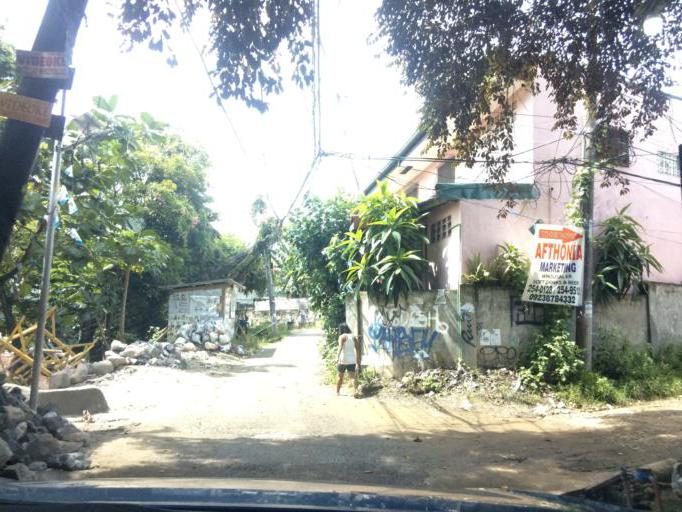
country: PH
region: Central Visayas
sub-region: Province of Cebu
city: Cebu City
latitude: 10.3205
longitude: 123.8967
